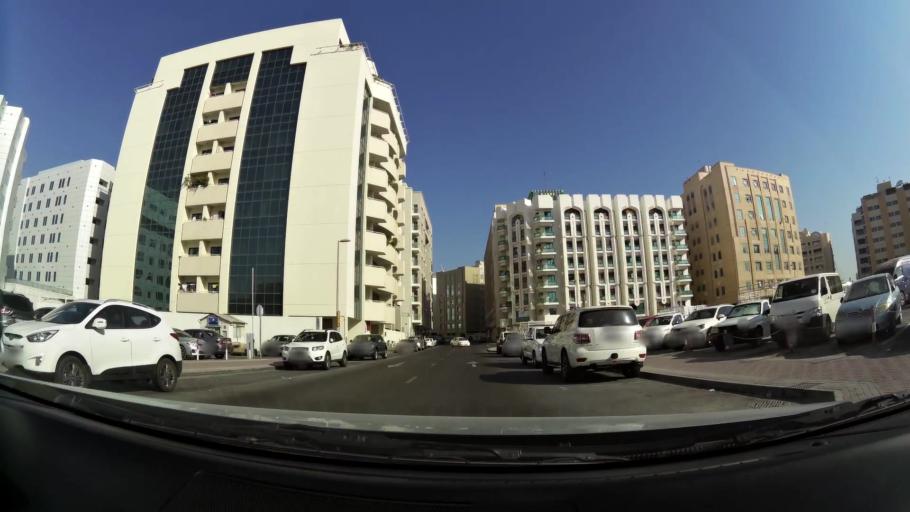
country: AE
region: Ash Shariqah
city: Sharjah
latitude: 25.2554
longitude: 55.2924
